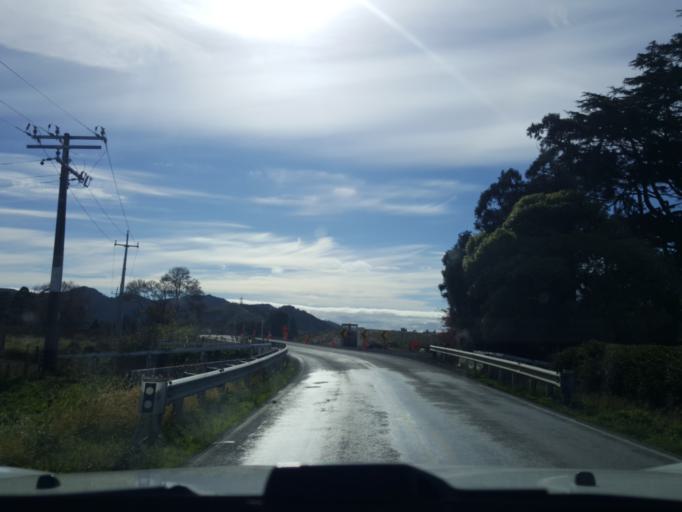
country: NZ
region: Waikato
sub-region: Waikato District
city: Ngaruawahia
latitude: -37.6005
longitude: 175.2024
